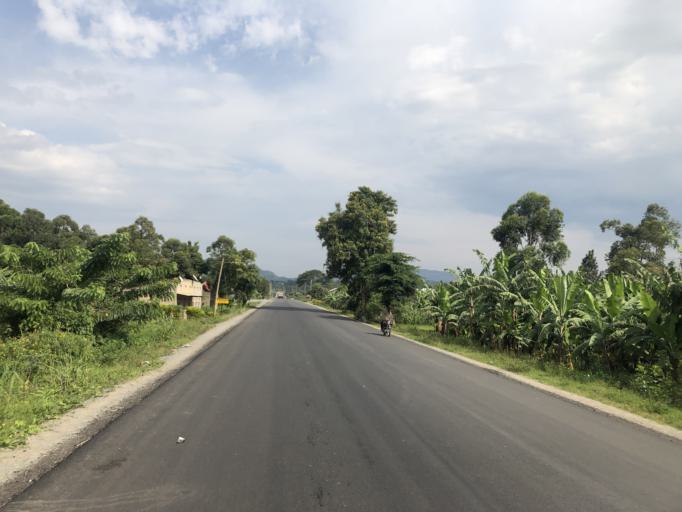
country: UG
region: Western Region
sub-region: Rubirizi District
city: Rubirizi
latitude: -0.2285
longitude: 30.0940
